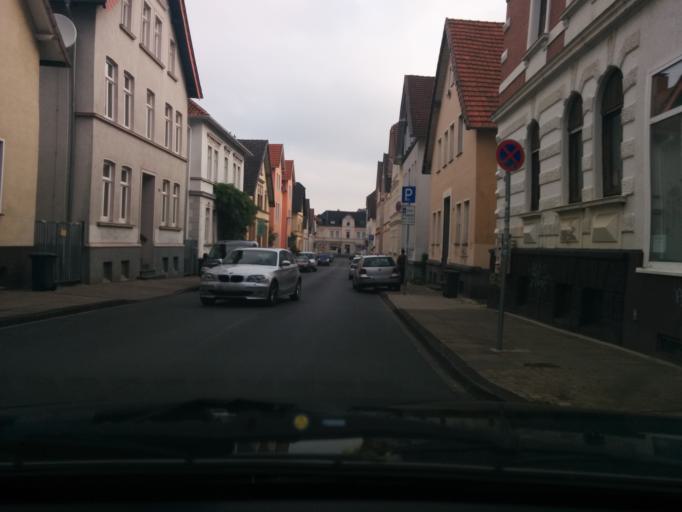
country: DE
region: North Rhine-Westphalia
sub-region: Regierungsbezirk Detmold
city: Bielefeld
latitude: 52.0296
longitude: 8.5228
